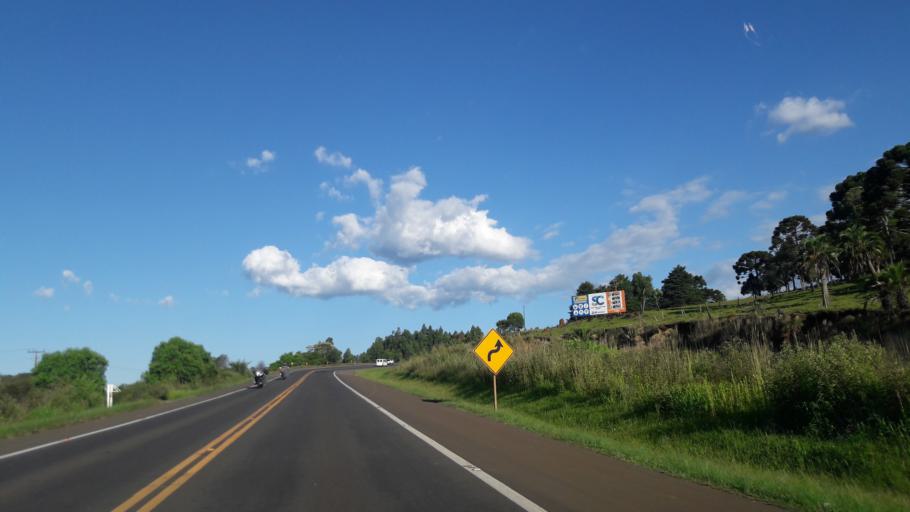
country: BR
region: Parana
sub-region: Guarapuava
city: Guarapuava
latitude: -25.3659
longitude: -51.3442
